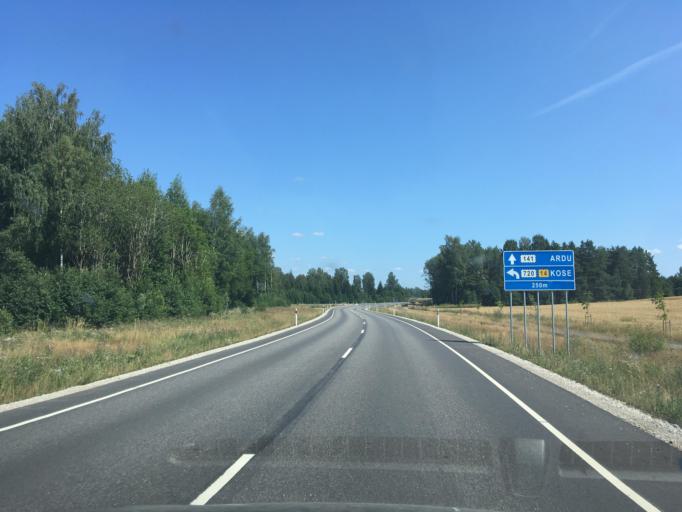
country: EE
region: Harju
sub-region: Anija vald
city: Kehra
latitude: 59.1053
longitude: 25.3216
